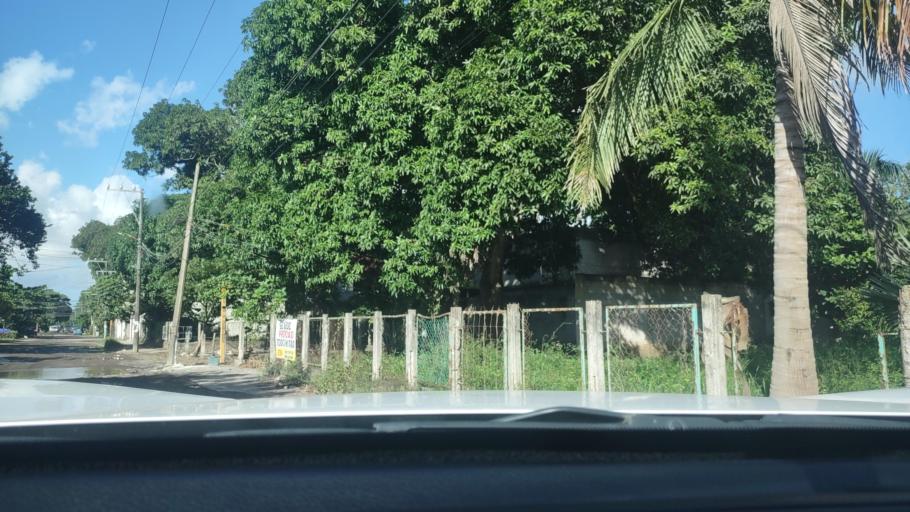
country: MX
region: Veracruz
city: El Tejar
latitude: 19.0711
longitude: -96.1586
